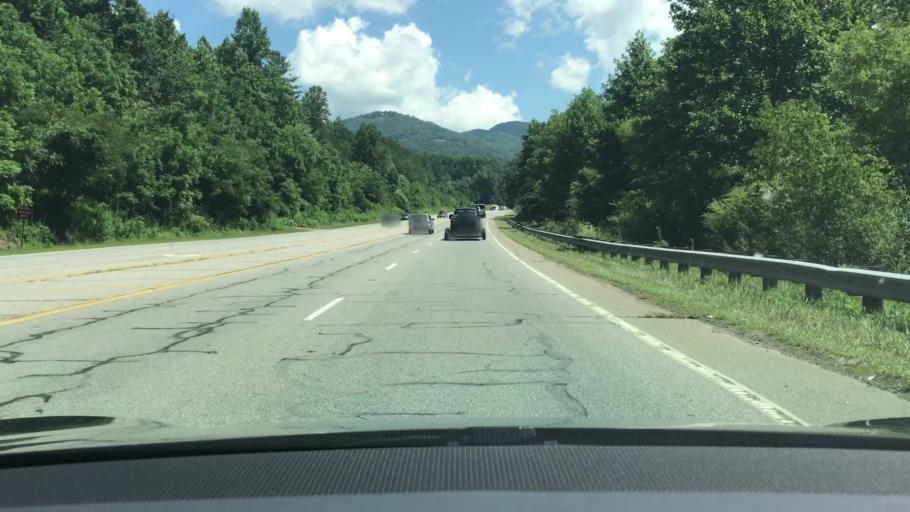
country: US
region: North Carolina
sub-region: Macon County
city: Franklin
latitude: 35.2283
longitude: -83.3514
